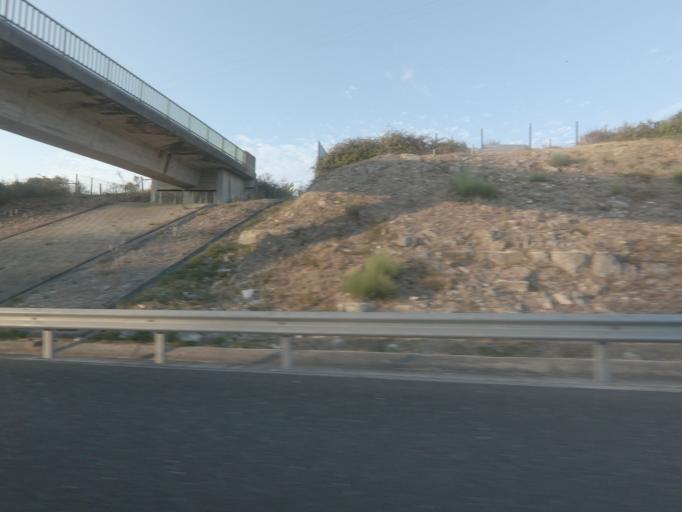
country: PT
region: Leiria
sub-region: Leiria
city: Santa Catarina da Serra
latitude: 39.7029
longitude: -8.7011
